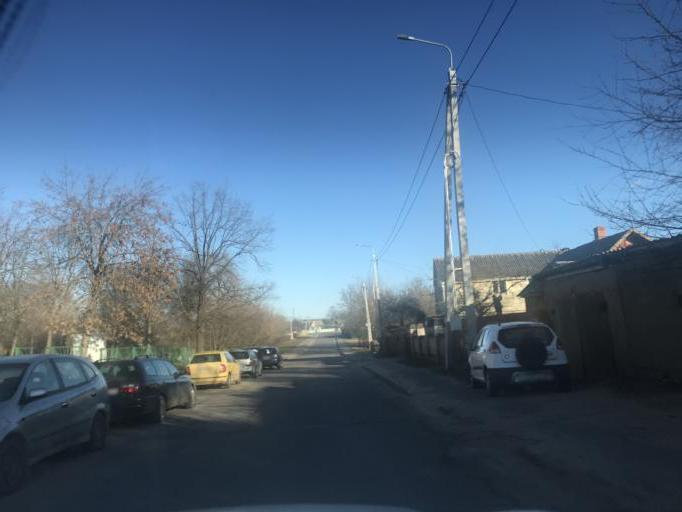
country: BY
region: Mogilev
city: Mahilyow
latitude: 53.9107
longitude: 30.3522
